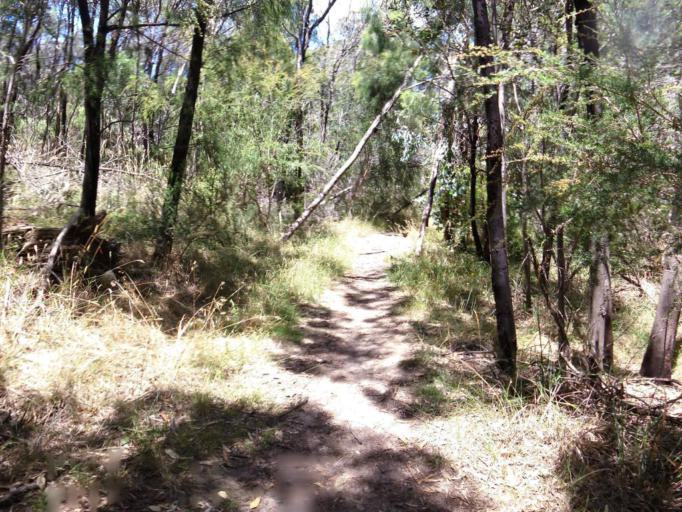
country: AU
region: Victoria
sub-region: Mornington Peninsula
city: Safety Beach
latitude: -38.2954
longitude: 145.0011
